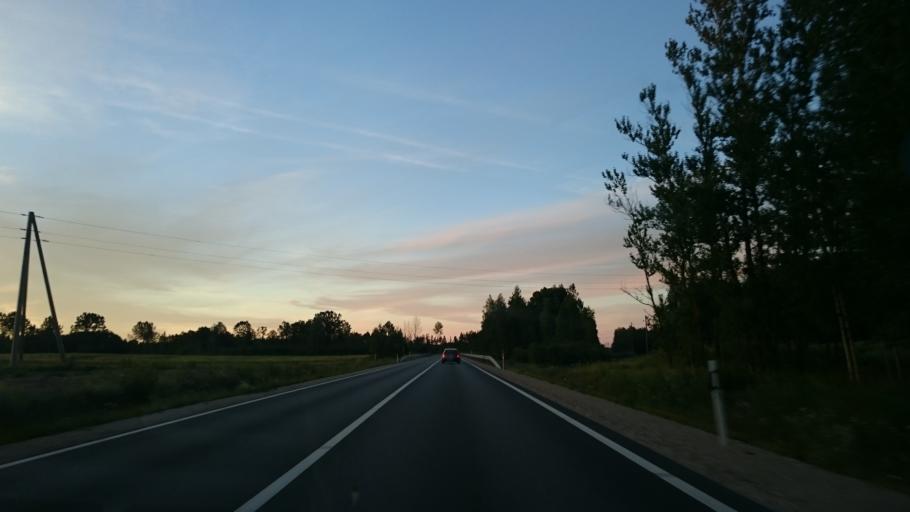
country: LV
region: Dobeles Rajons
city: Dobele
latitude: 56.7150
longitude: 23.1901
